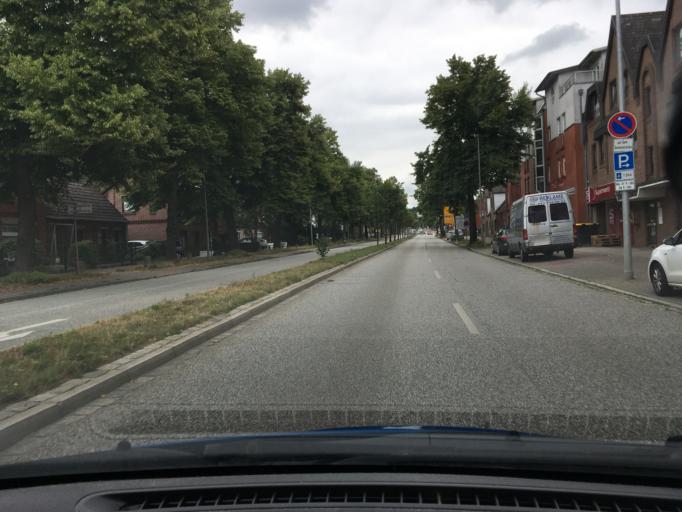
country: DE
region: Schleswig-Holstein
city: Geesthacht
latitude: 53.4371
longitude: 10.3692
